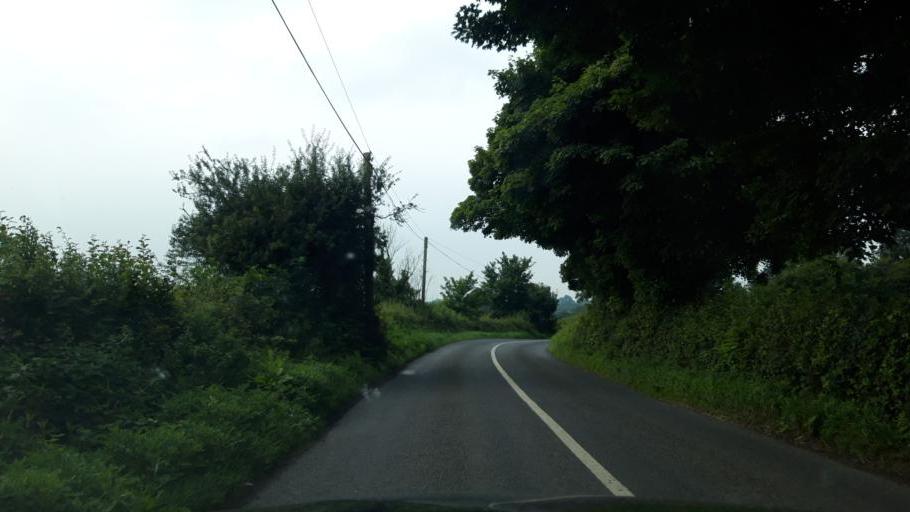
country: IE
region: Munster
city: Fethard
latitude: 52.5859
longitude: -7.5948
